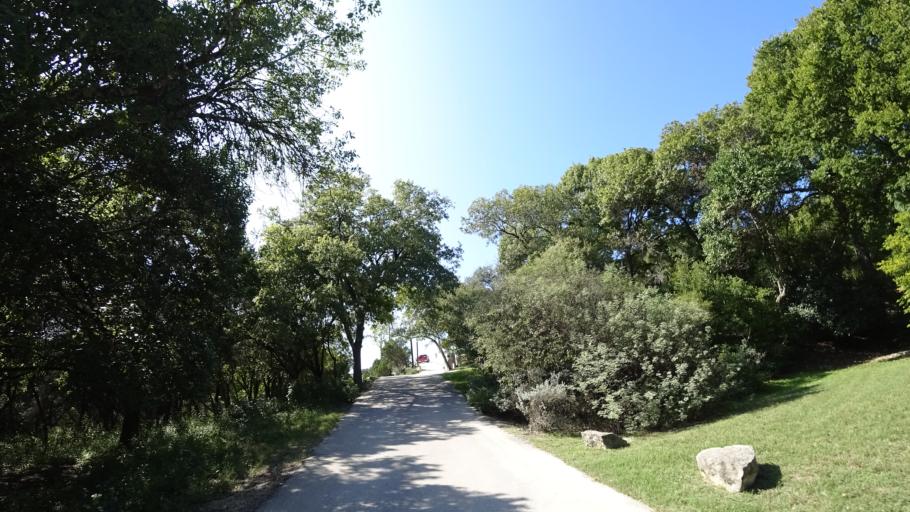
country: US
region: Texas
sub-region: Travis County
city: West Lake Hills
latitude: 30.2949
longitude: -97.8063
